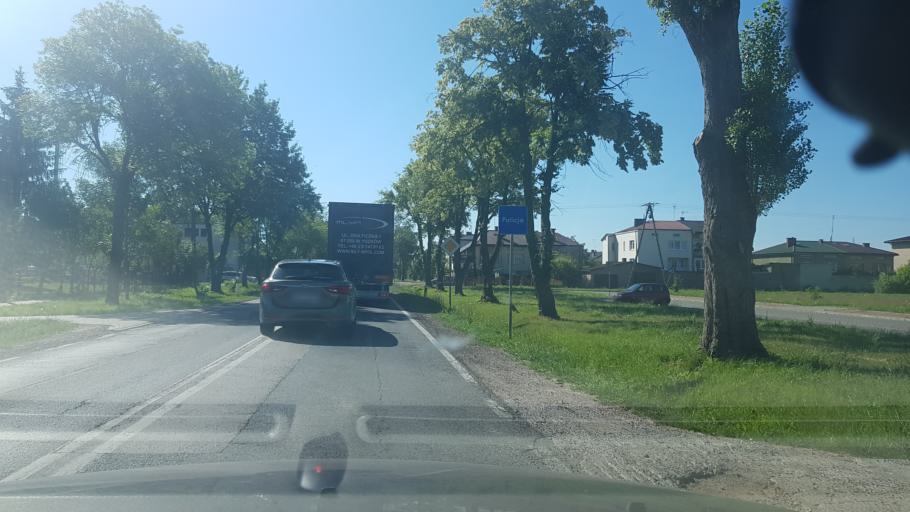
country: PL
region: Masovian Voivodeship
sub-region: Powiat wegrowski
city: Lochow
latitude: 52.5287
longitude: 21.6843
